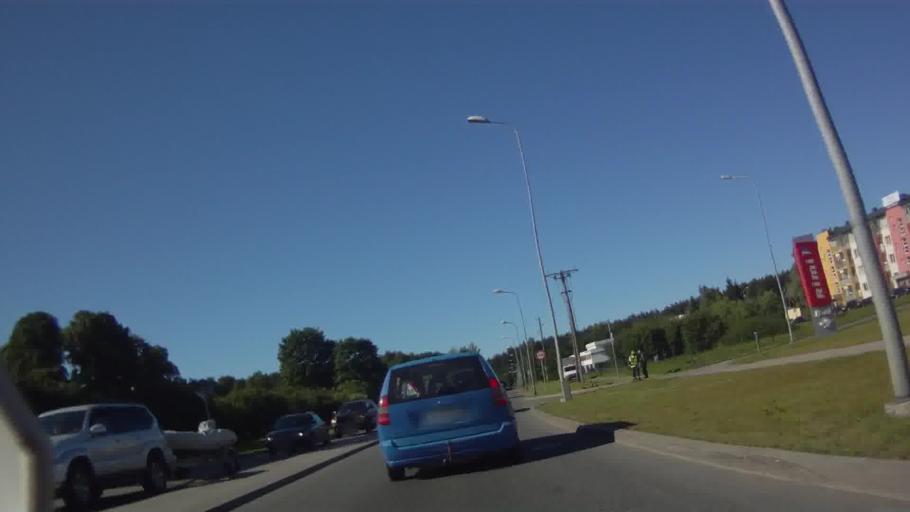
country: LV
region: Stopini
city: Ulbroka
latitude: 56.9571
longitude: 24.2523
